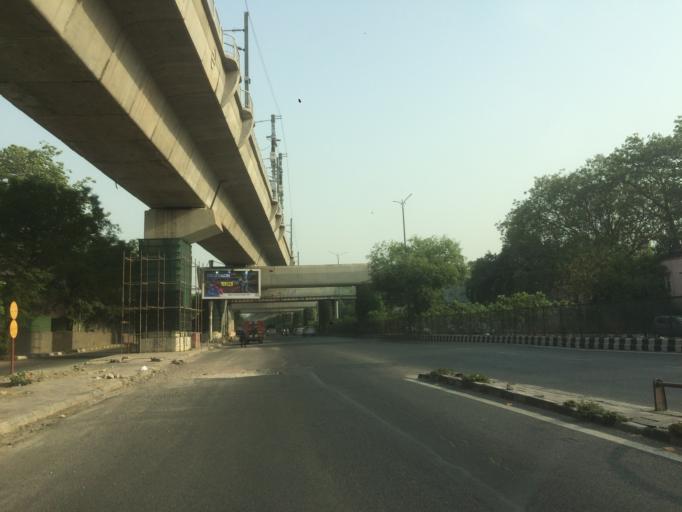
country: IN
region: NCT
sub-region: Central Delhi
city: Karol Bagh
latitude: 28.5802
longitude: 77.1749
